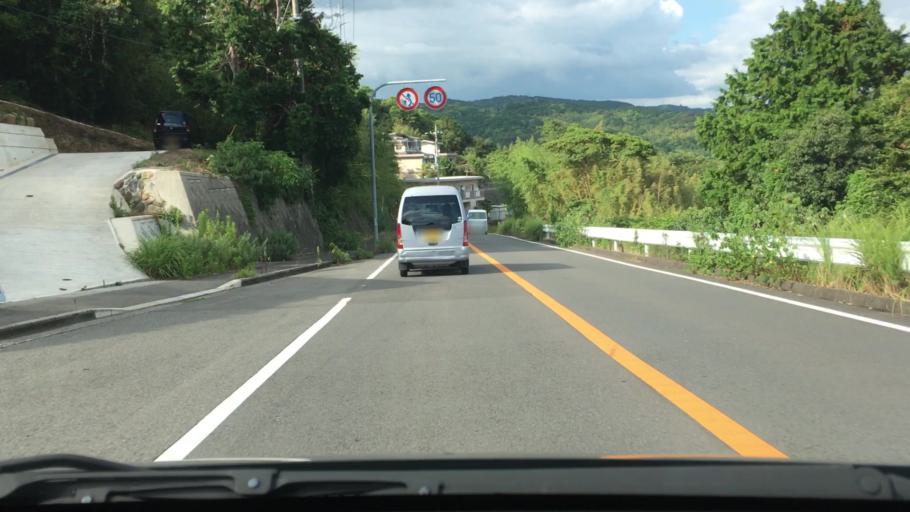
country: JP
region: Nagasaki
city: Togitsu
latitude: 32.8378
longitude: 129.7090
